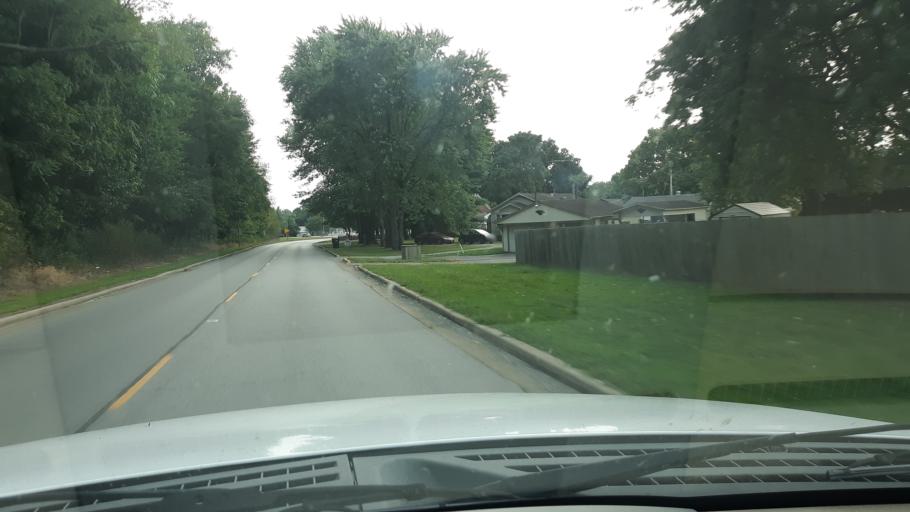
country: US
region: Illinois
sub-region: Edwards County
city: Grayville
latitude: 38.1669
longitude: -88.0610
